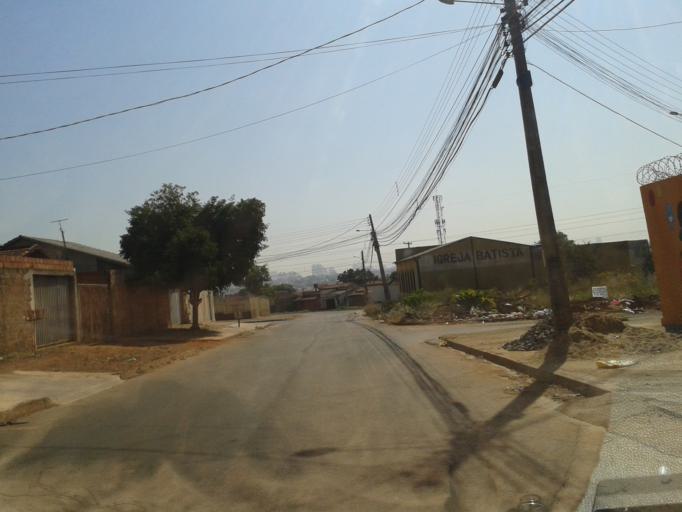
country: BR
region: Goias
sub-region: Aparecida De Goiania
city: Aparecida de Goiania
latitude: -16.7758
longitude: -49.2944
